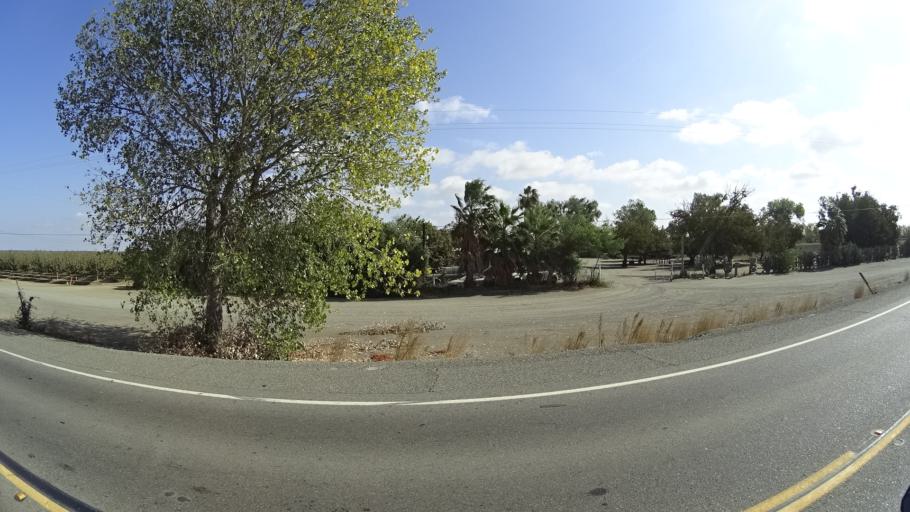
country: US
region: California
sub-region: Yolo County
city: Woodland
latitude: 38.7287
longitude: -121.7299
